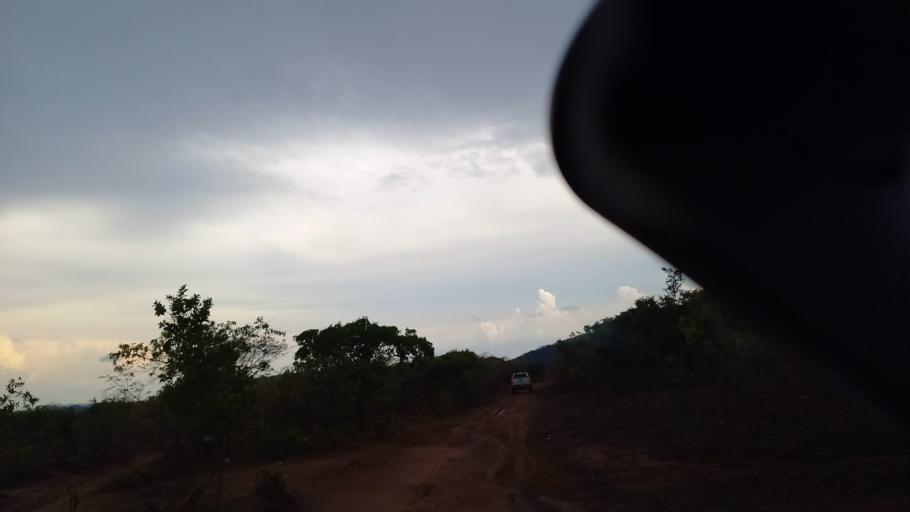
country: ZM
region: Lusaka
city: Kafue
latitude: -16.0266
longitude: 28.2987
